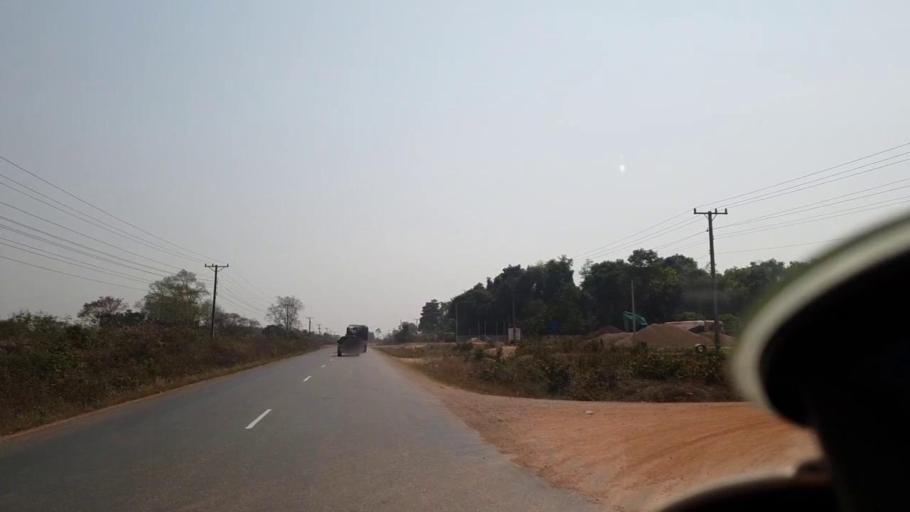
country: TH
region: Nong Khai
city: Phon Phisai
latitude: 18.0747
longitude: 102.9684
